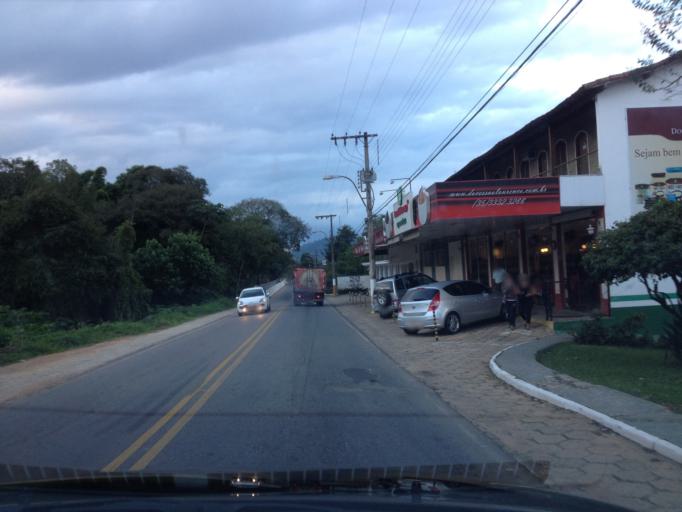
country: BR
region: Minas Gerais
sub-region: Sao Lourenco
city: Sao Lourenco
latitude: -22.1012
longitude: -45.0515
